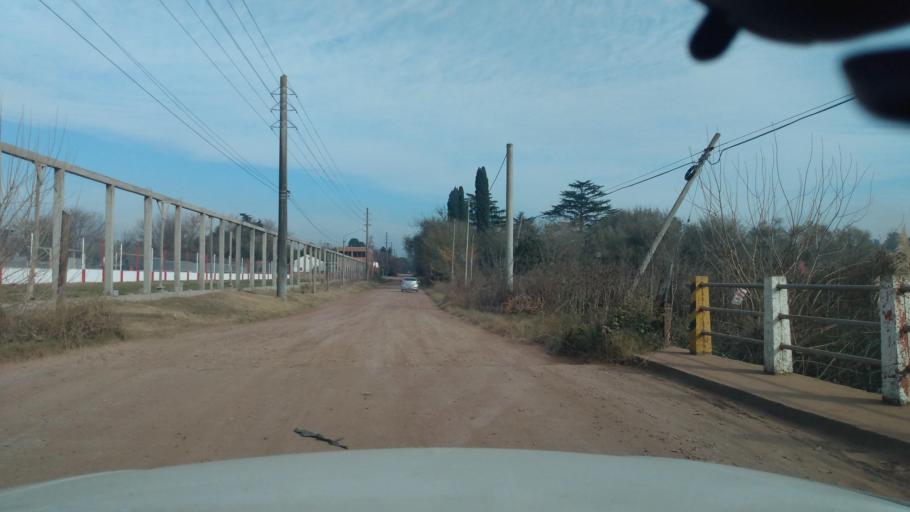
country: AR
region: Buenos Aires
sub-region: Partido de Lujan
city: Lujan
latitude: -34.5863
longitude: -59.1225
